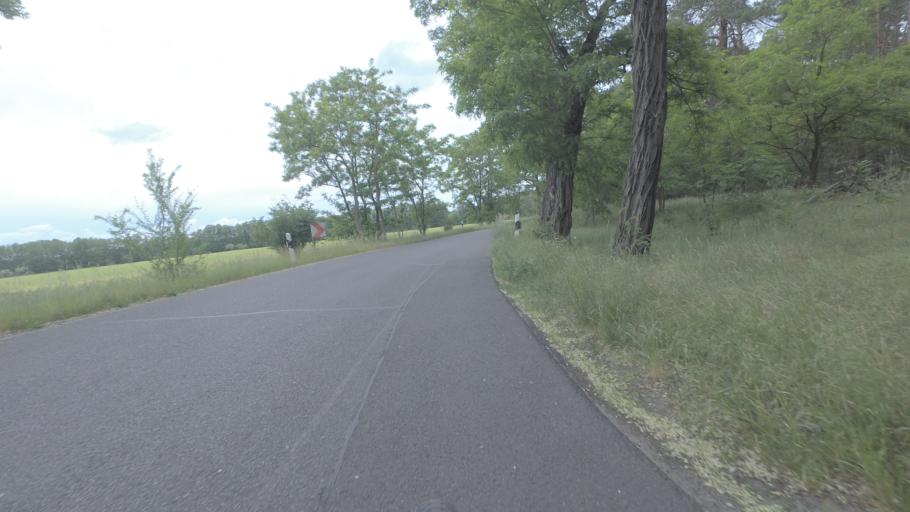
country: DE
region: Brandenburg
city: Bestensee
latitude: 52.2612
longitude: 13.7610
